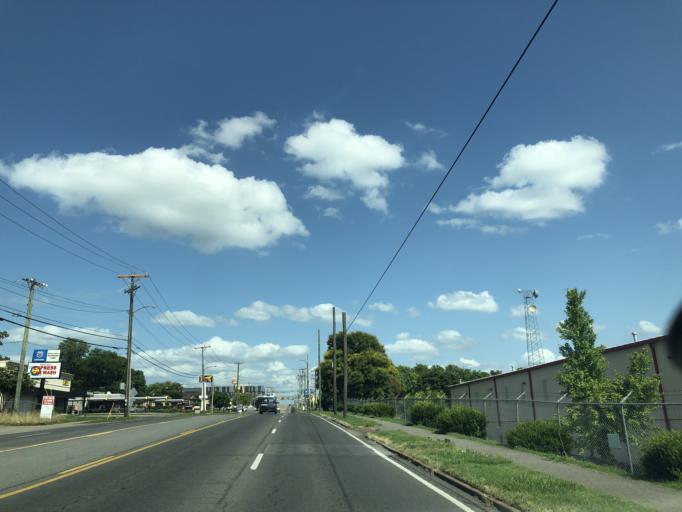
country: US
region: Tennessee
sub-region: Davidson County
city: Nashville
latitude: 36.1438
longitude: -86.7473
